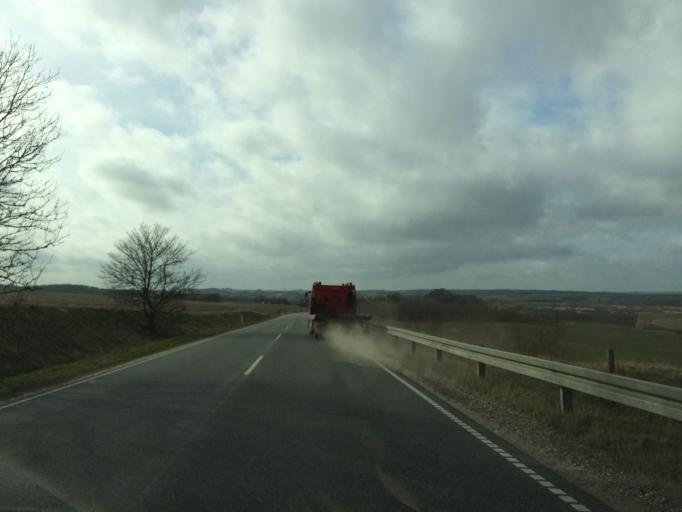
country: DK
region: Central Jutland
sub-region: Randers Kommune
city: Langa
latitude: 56.4810
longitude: 9.8794
